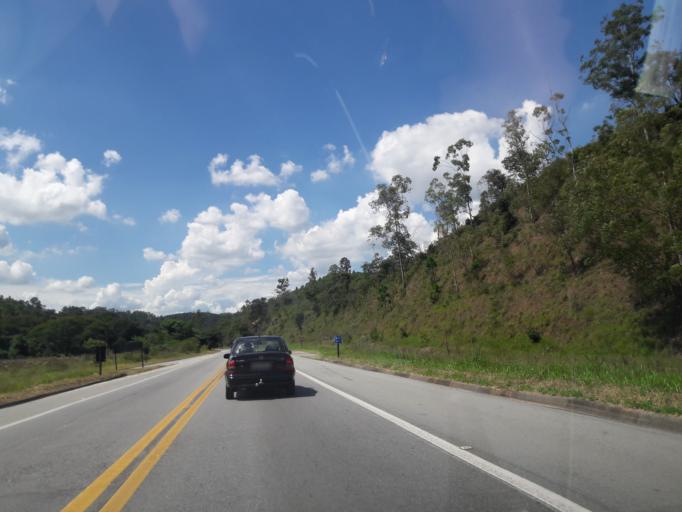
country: BR
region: Sao Paulo
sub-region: Francisco Morato
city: Francisco Morato
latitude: -23.2840
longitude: -46.7982
